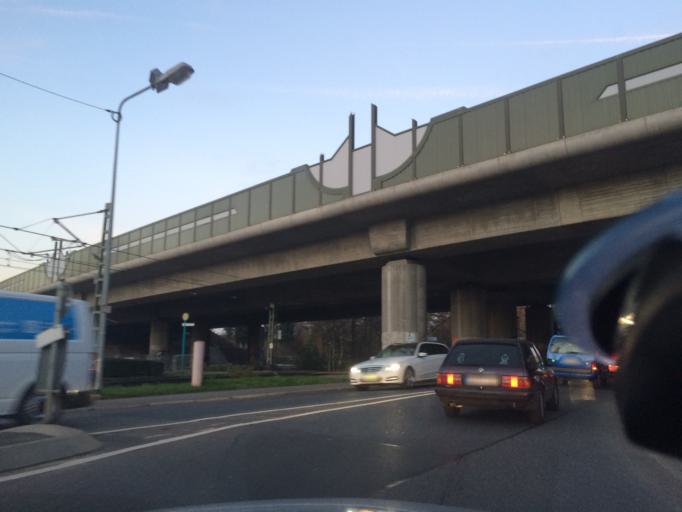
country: DE
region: Hesse
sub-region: Regierungsbezirk Darmstadt
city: Frankfurt am Main
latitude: 50.1271
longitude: 8.7246
